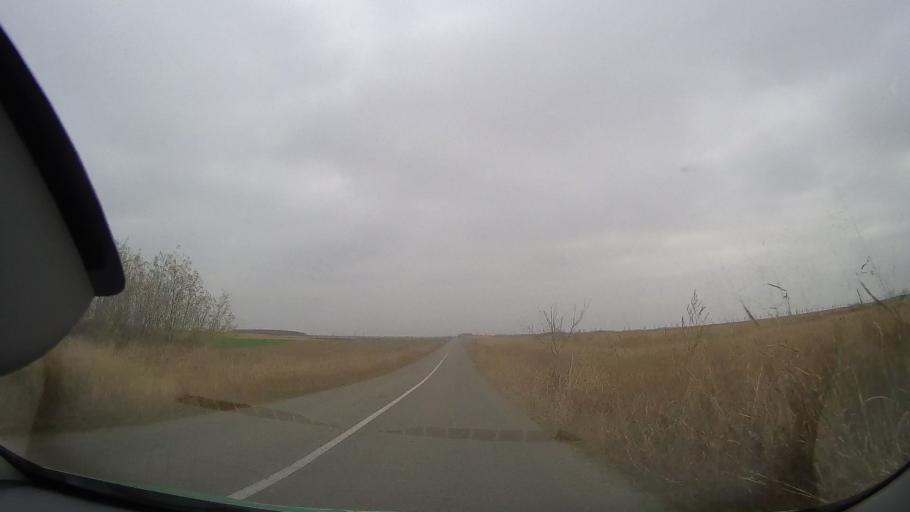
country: RO
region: Buzau
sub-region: Comuna Scutelnici
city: Scutelnici
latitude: 44.8735
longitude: 26.8849
